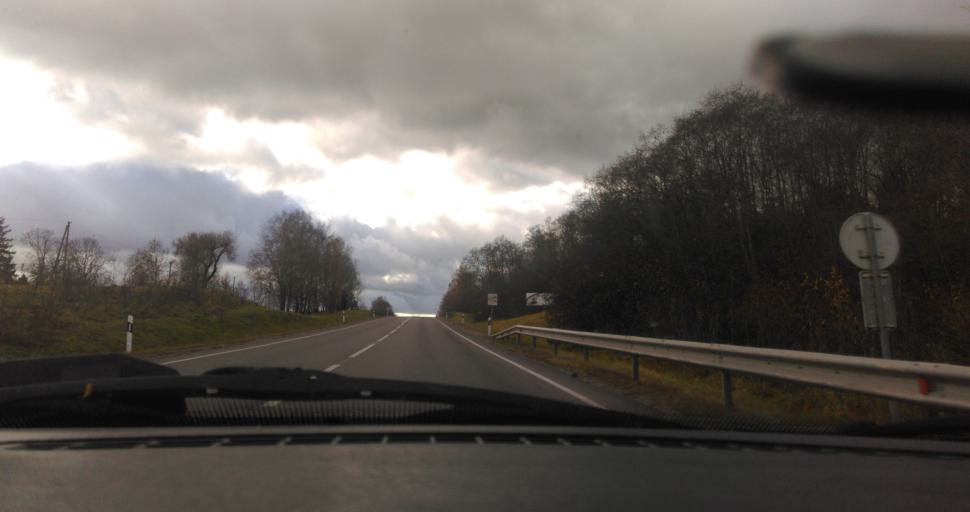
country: LT
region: Utenos apskritis
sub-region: Utena
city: Utena
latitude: 55.5151
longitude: 25.6496
